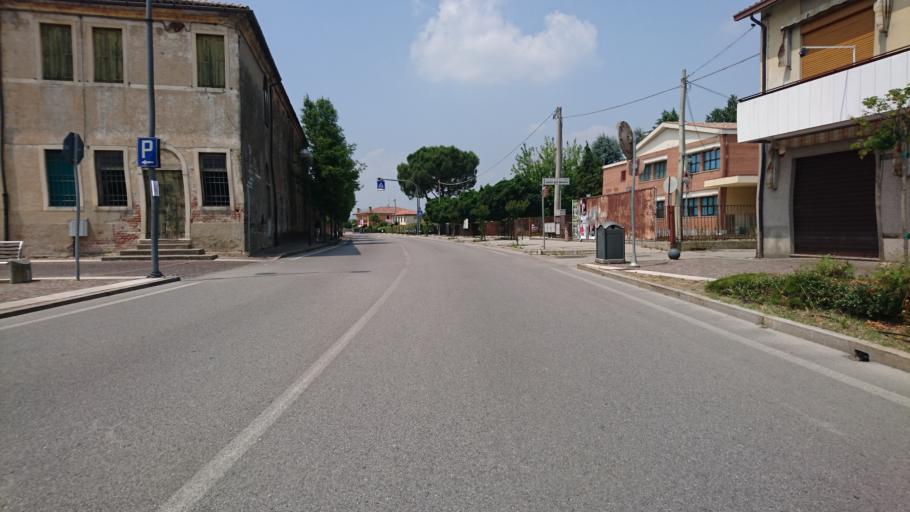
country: IT
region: Veneto
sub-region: Provincia di Padova
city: Cartura
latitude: 45.2686
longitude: 11.8598
